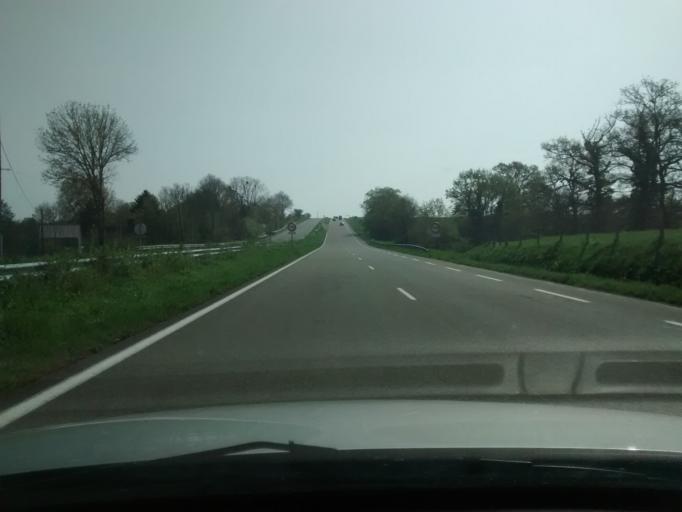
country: FR
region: Pays de la Loire
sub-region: Departement de la Mayenne
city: Argentre
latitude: 48.0663
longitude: -0.6499
